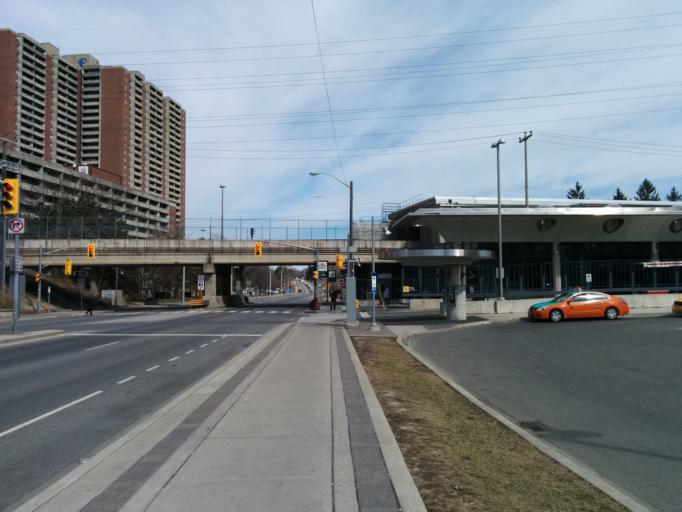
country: CA
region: Ontario
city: Scarborough
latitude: 43.6942
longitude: -79.2893
